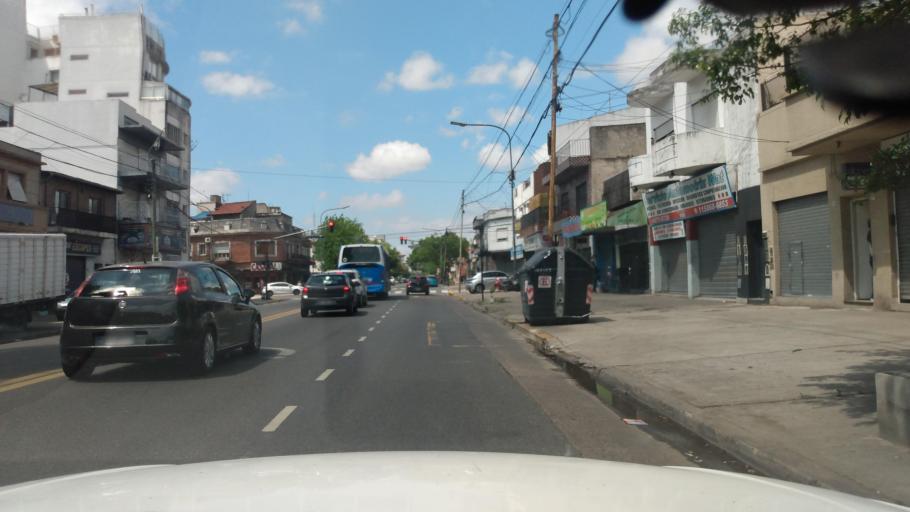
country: AR
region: Buenos Aires
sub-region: Partido de General San Martin
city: General San Martin
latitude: -34.5749
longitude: -58.5013
